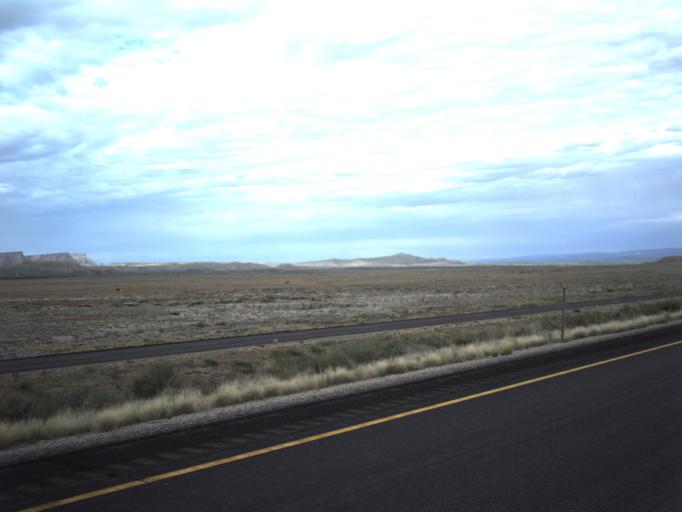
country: US
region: Utah
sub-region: Grand County
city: Moab
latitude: 38.9492
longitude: -109.6749
